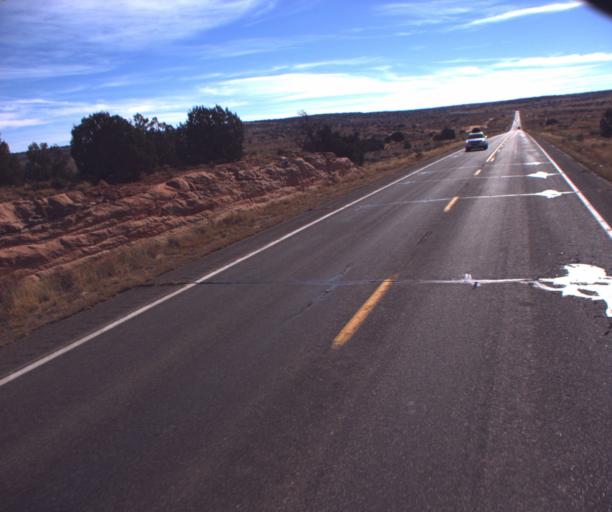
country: US
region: Arizona
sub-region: Coconino County
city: Kaibito
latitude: 36.5939
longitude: -111.1618
